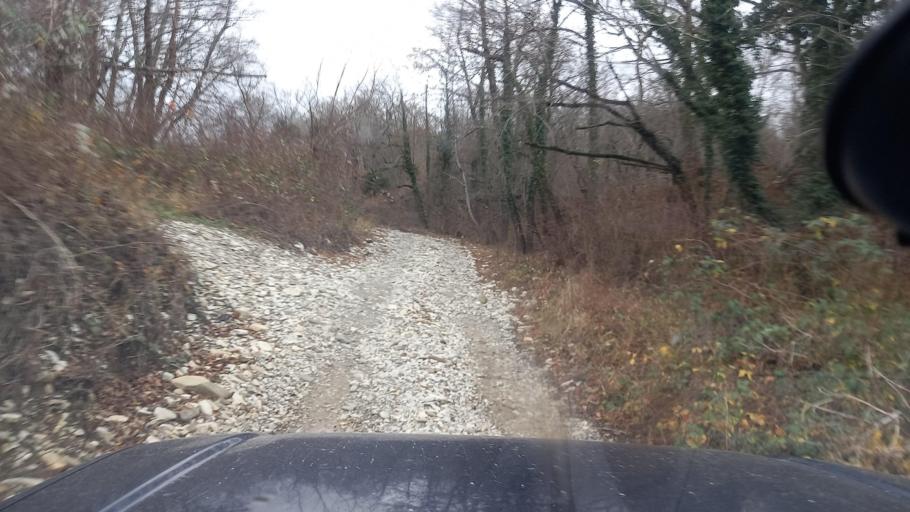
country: RU
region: Krasnodarskiy
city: Pshada
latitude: 44.4950
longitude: 38.4219
